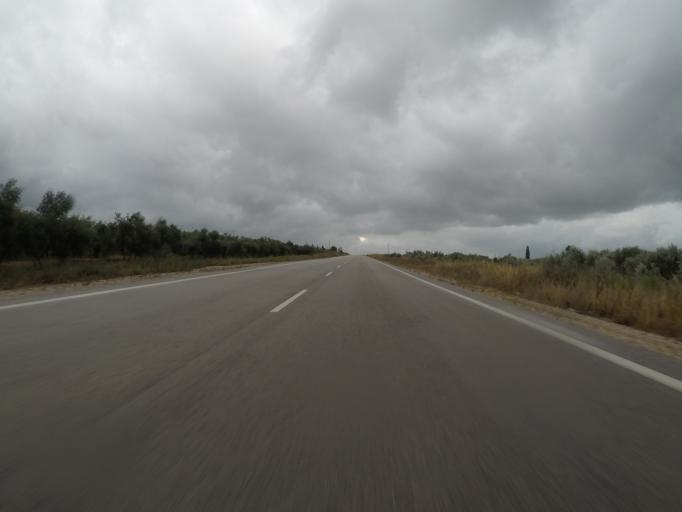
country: GR
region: Peloponnese
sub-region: Nomos Messinias
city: Gargalianoi
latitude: 37.0183
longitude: 21.6415
